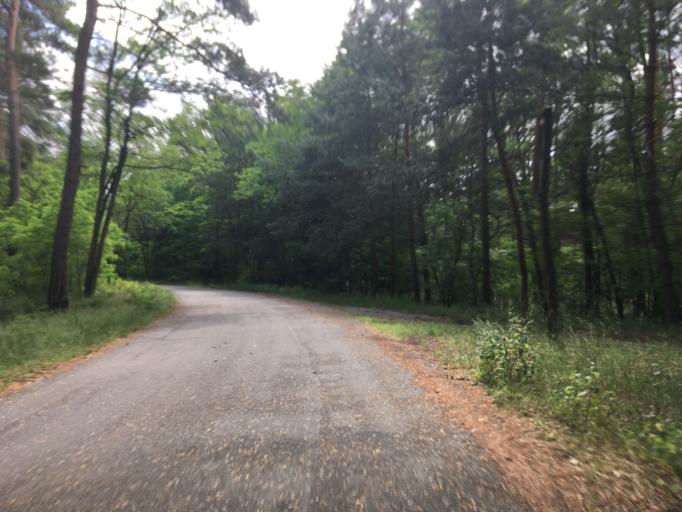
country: DE
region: Berlin
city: Muggelheim
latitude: 52.4044
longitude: 13.6472
